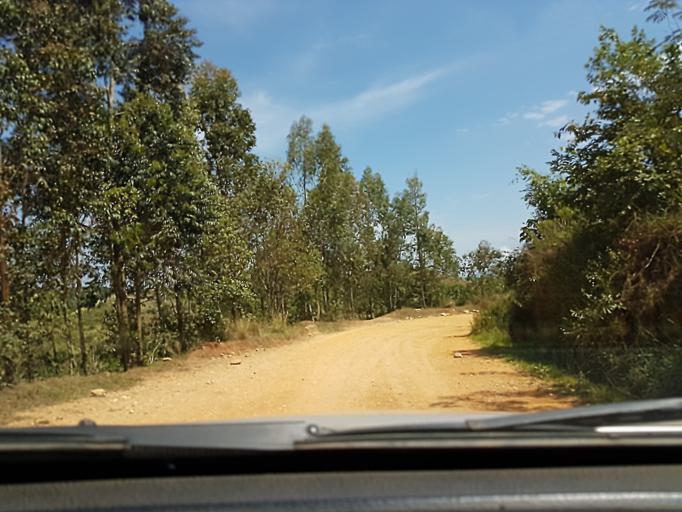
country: RW
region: Western Province
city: Cyangugu
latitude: -2.7024
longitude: 28.9128
